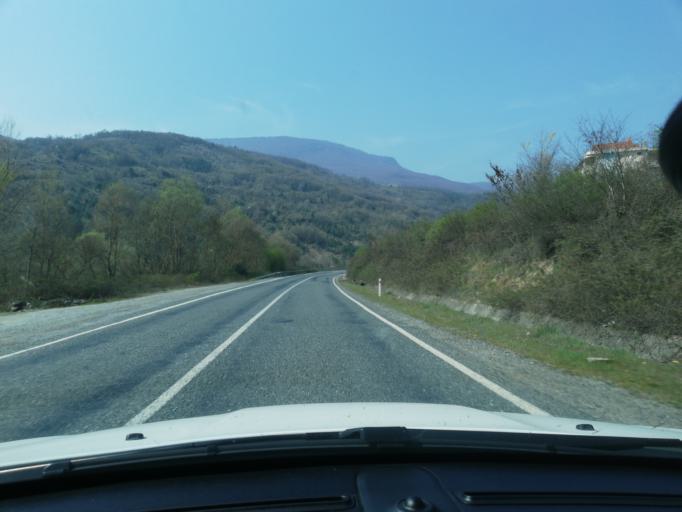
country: TR
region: Karabuk
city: Yenice
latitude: 41.2124
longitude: 32.2743
